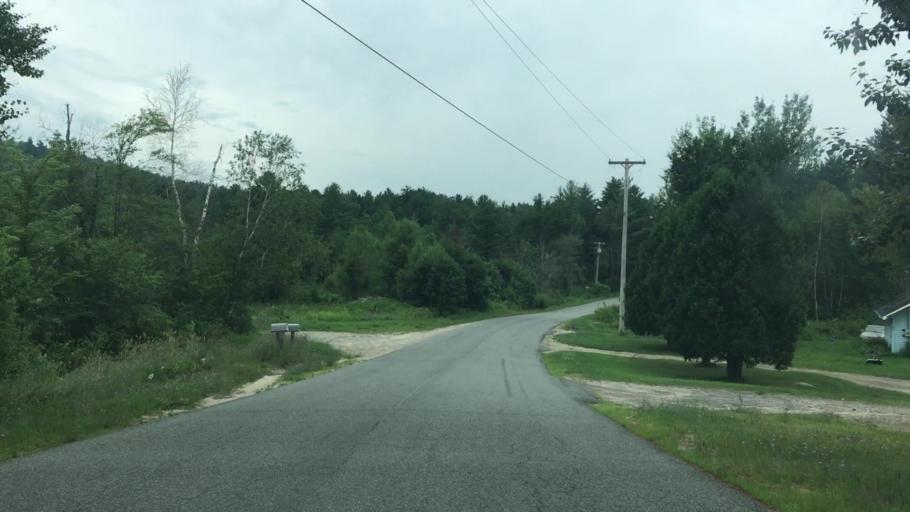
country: US
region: New York
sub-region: Essex County
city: Keeseville
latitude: 44.4429
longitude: -73.6092
